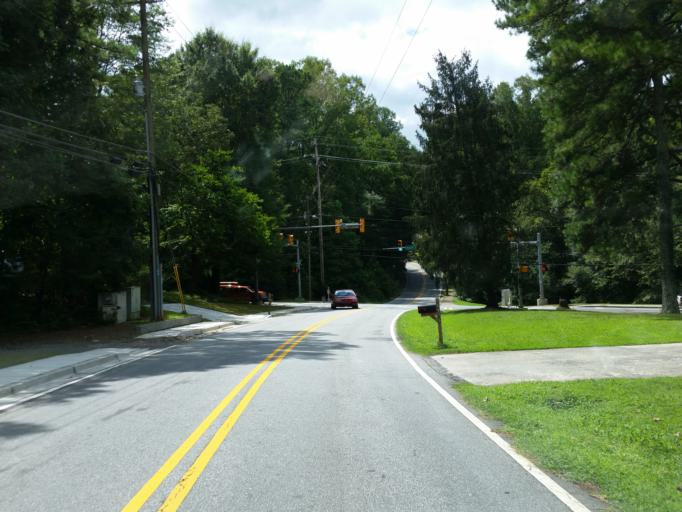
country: US
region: Georgia
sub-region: Cobb County
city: Marietta
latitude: 33.9519
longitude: -84.4772
